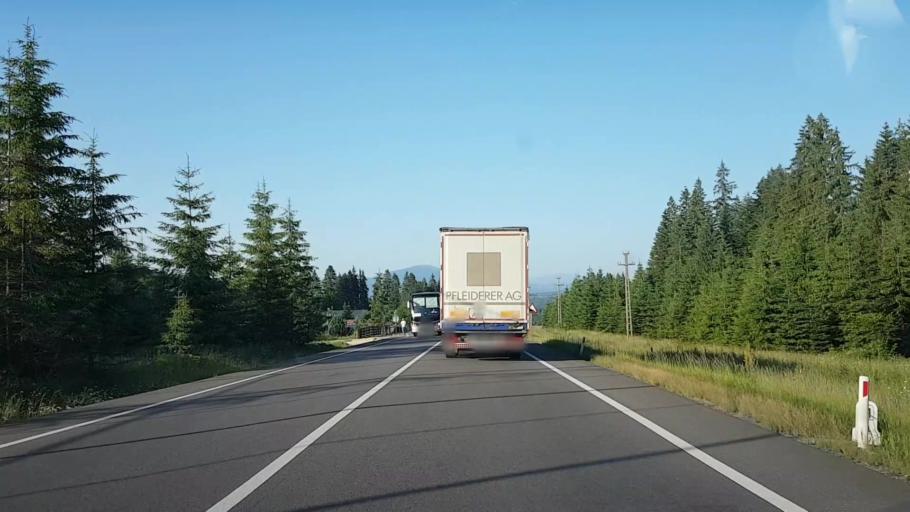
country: RO
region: Suceava
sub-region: Comuna Poiana Stampei
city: Poiana Stampei
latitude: 47.2951
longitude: 25.0839
